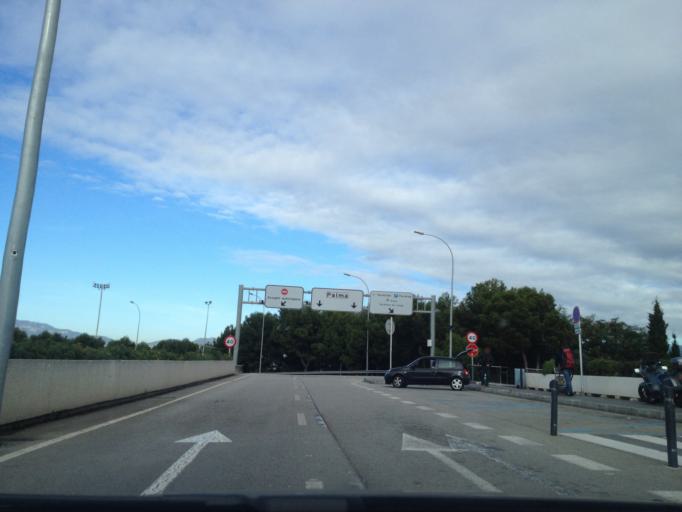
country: ES
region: Balearic Islands
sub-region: Illes Balears
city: s'Arenal
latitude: 39.5484
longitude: 2.7296
